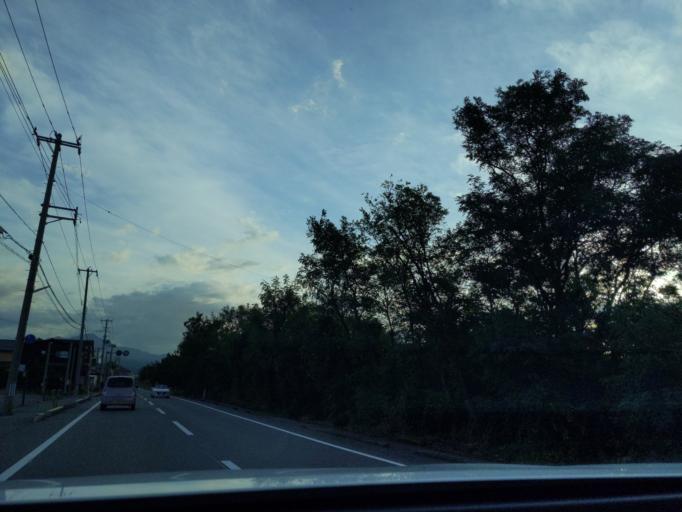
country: JP
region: Niigata
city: Kashiwazaki
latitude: 37.3803
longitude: 138.5587
